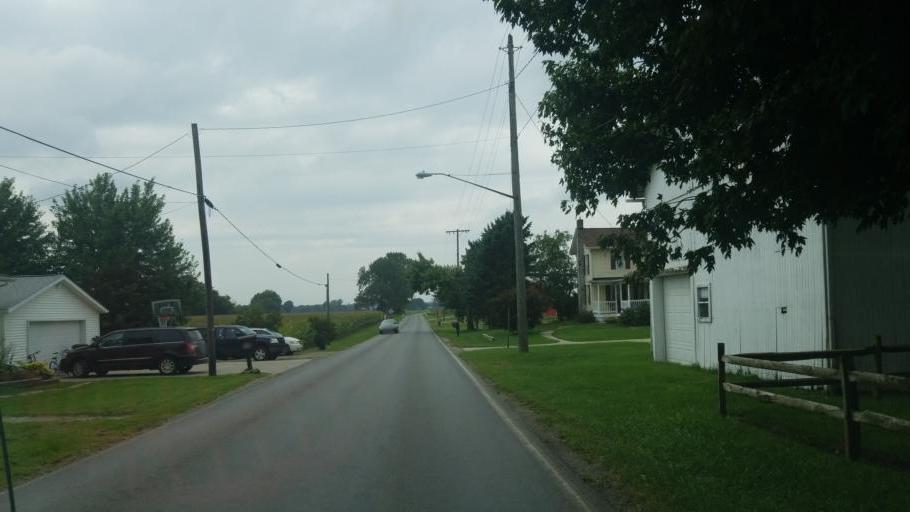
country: US
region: Ohio
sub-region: Medina County
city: Seville
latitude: 40.9604
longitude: -81.8424
